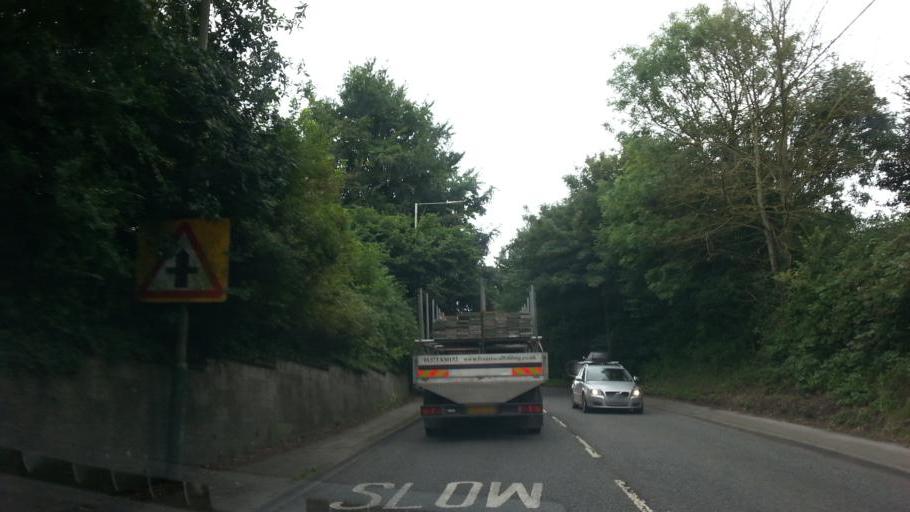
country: GB
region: England
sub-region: Wiltshire
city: Westbury
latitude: 51.2490
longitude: -2.1895
